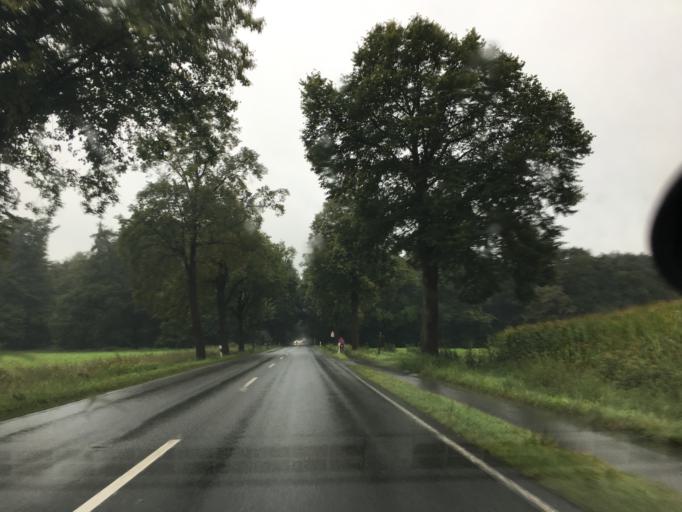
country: DE
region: North Rhine-Westphalia
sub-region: Regierungsbezirk Detmold
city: Guetersloh
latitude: 51.8802
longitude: 8.3539
